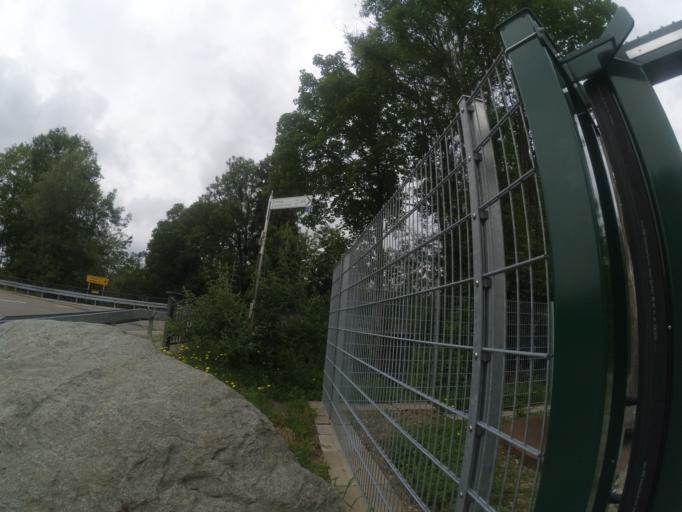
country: DE
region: Baden-Wuerttemberg
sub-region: Tuebingen Region
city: Wangen im Allgau
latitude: 47.7076
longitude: 9.8315
